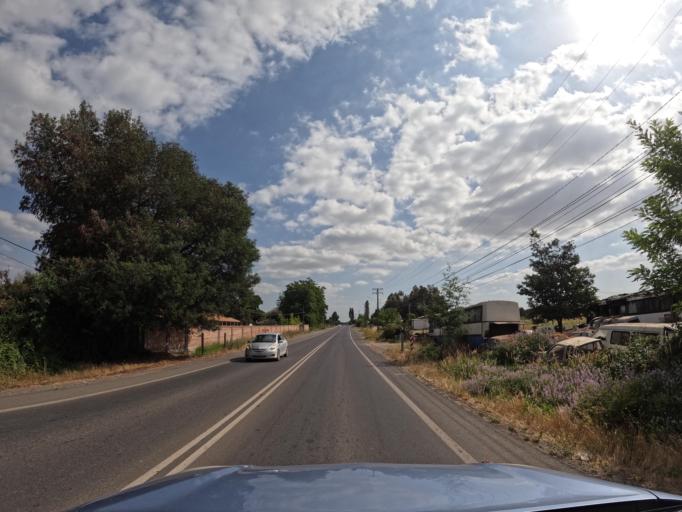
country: CL
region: Maule
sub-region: Provincia de Curico
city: Molina
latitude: -35.1463
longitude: -71.2804
